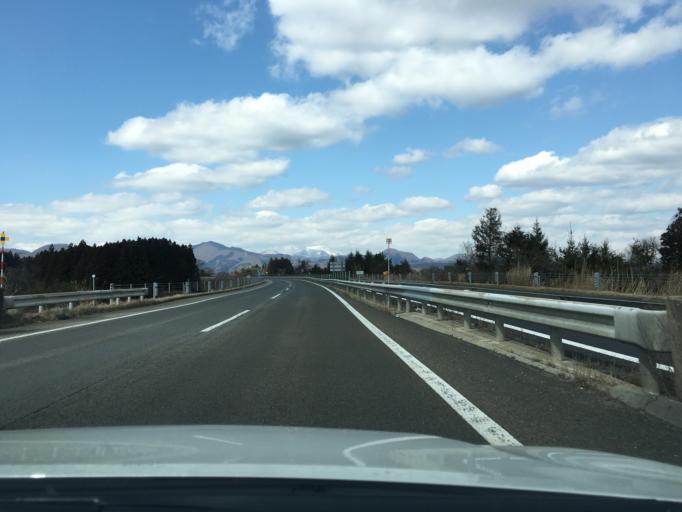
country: JP
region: Miyagi
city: Okawara
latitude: 38.1689
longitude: 140.6386
